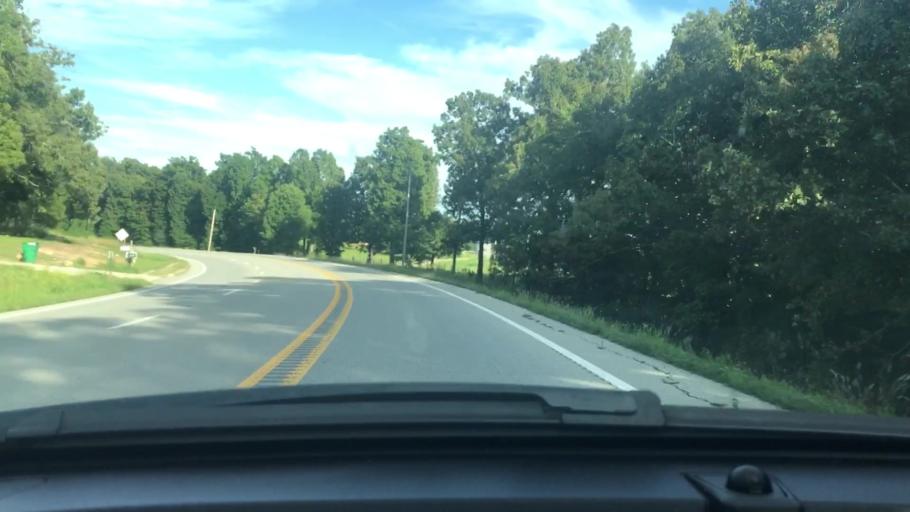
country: US
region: Arkansas
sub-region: Sharp County
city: Cherokee Village
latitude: 36.2718
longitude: -91.3701
